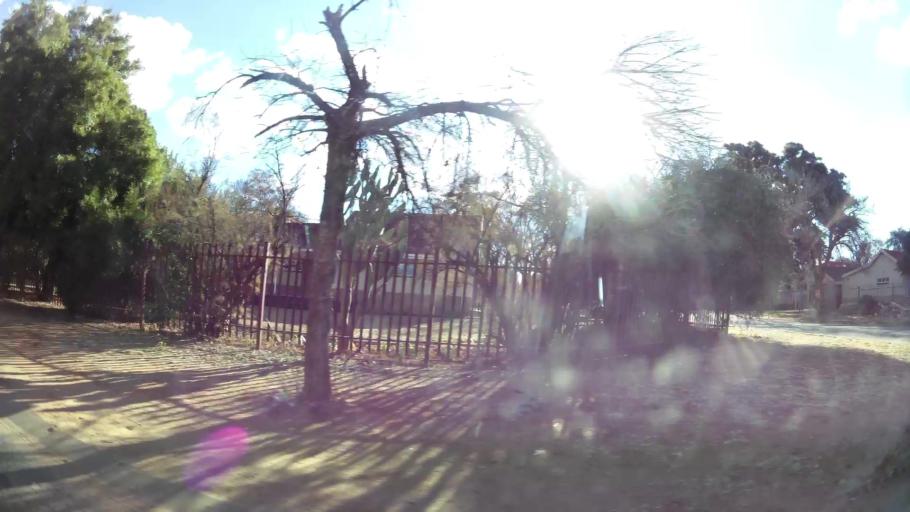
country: ZA
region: North-West
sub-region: Dr Kenneth Kaunda District Municipality
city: Klerksdorp
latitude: -26.8422
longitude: 26.6567
